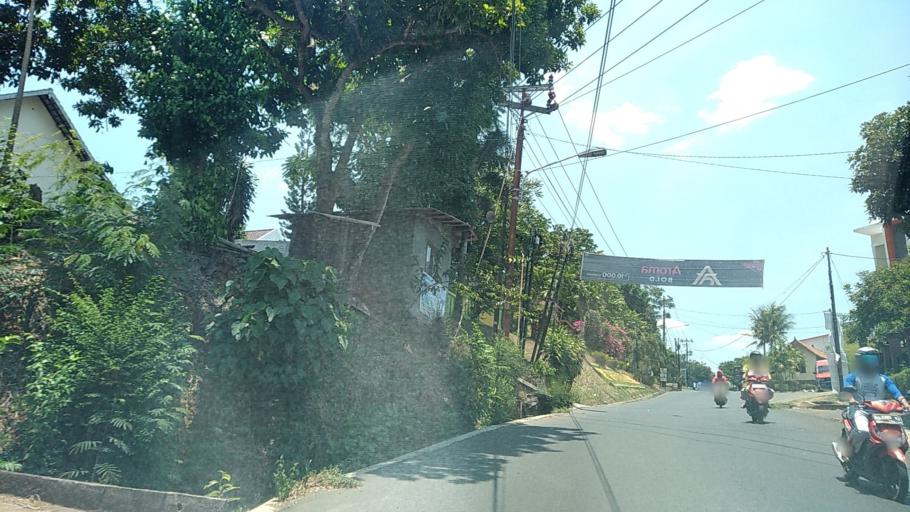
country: ID
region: Central Java
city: Ungaran
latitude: -7.0771
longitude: 110.4215
